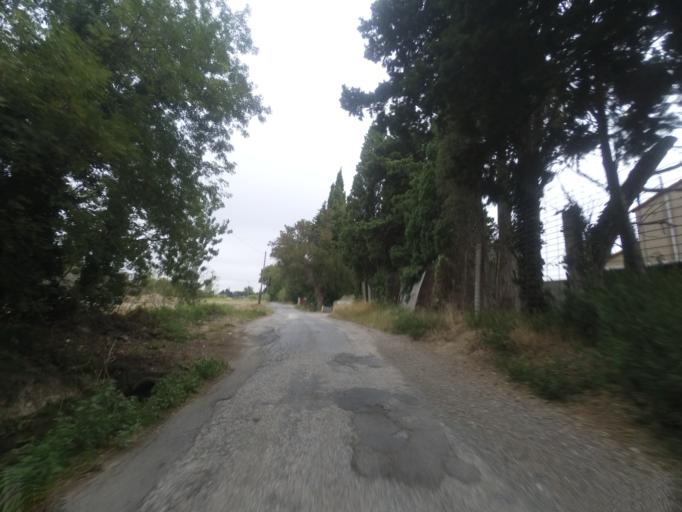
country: FR
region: Languedoc-Roussillon
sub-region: Departement des Pyrenees-Orientales
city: Baho
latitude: 42.6977
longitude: 2.8321
